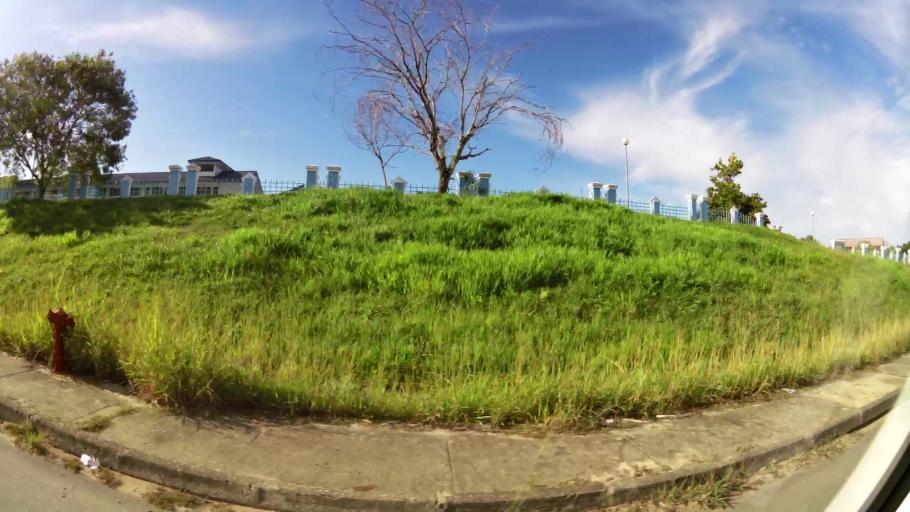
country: BN
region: Brunei and Muara
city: Bandar Seri Begawan
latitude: 4.9722
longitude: 114.9686
